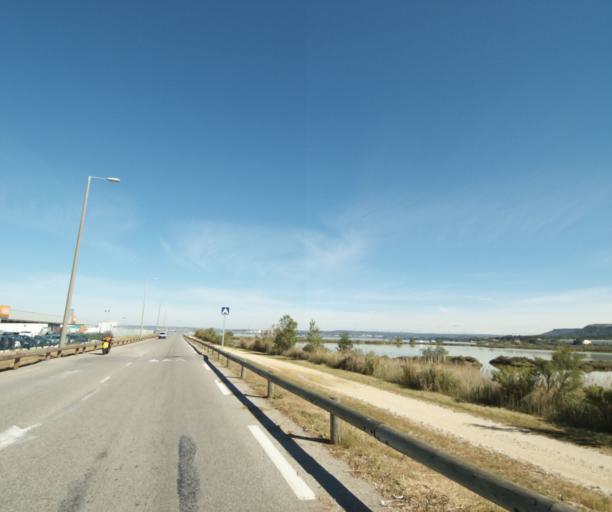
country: FR
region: Provence-Alpes-Cote d'Azur
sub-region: Departement des Bouches-du-Rhone
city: Vitrolles
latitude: 43.4477
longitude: 5.2251
